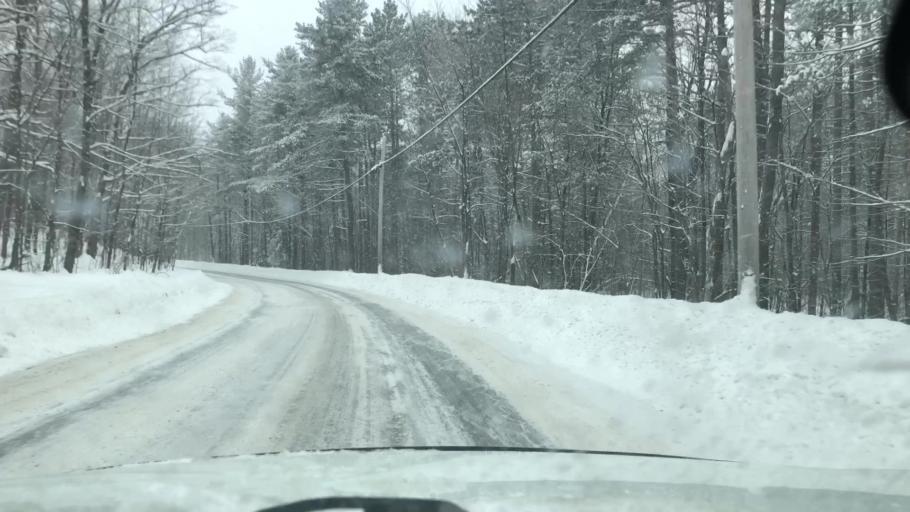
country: CA
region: Quebec
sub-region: Outaouais
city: Gatineau
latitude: 45.5109
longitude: -75.8325
